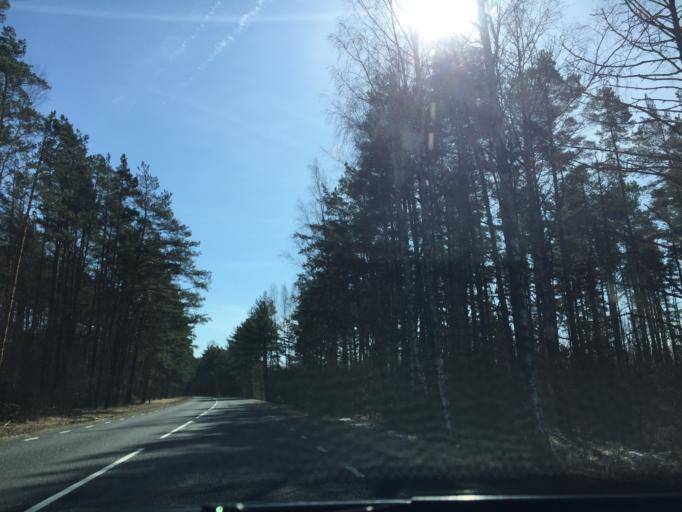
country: EE
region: Laeaene
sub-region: Lihula vald
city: Lihula
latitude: 58.5585
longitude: 23.8347
